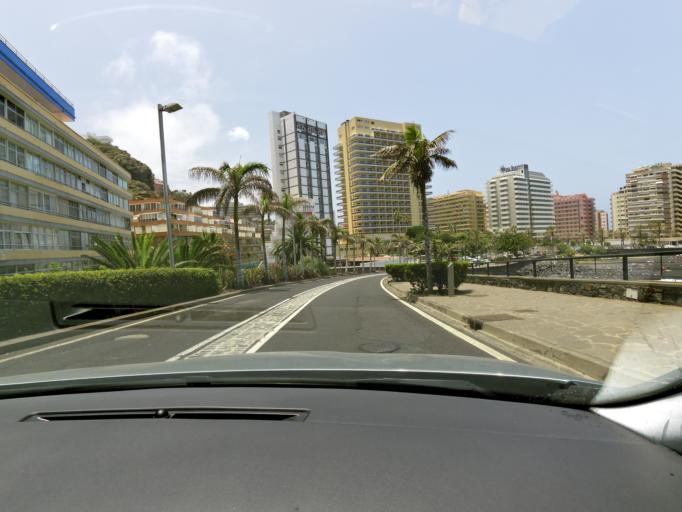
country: ES
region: Canary Islands
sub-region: Provincia de Santa Cruz de Tenerife
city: Puerto de la Cruz
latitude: 28.4164
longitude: -16.5395
